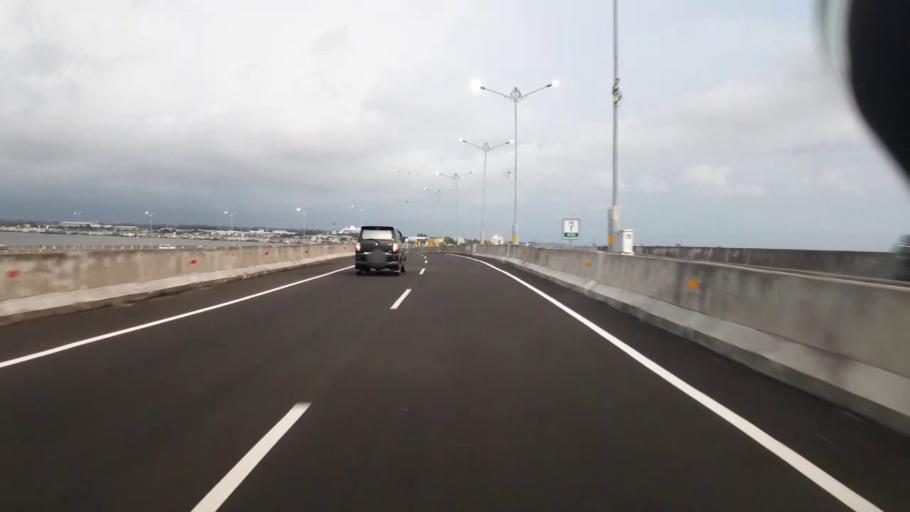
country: ID
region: Bali
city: Kelanabian
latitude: -8.7449
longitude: 115.1957
